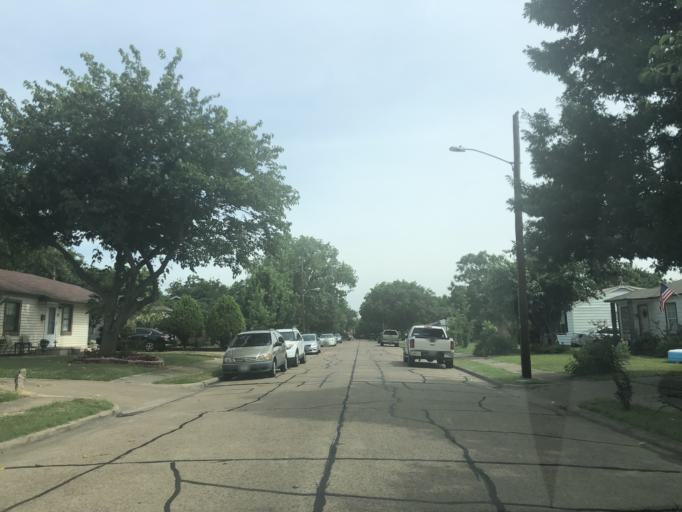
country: US
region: Texas
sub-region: Dallas County
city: Irving
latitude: 32.8104
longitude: -96.9724
